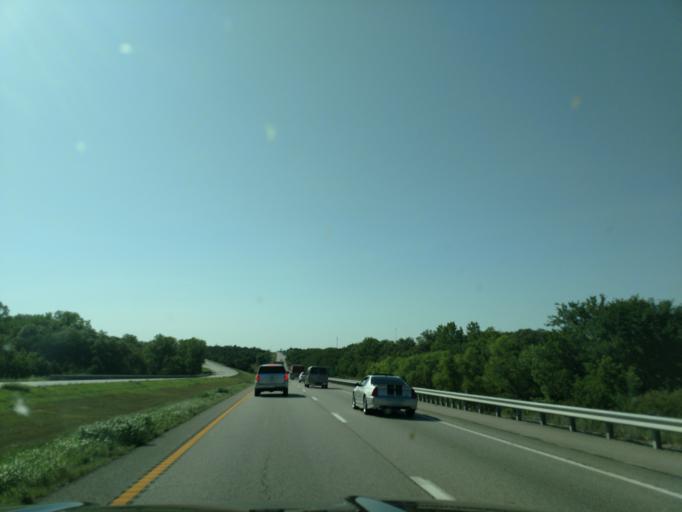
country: US
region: Missouri
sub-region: Andrew County
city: Country Club Village
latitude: 39.8798
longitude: -94.8458
